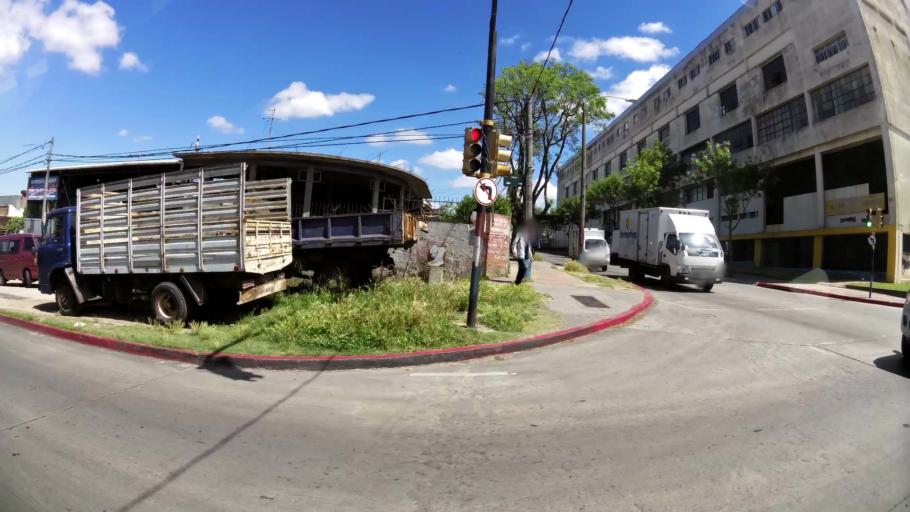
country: UY
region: Montevideo
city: Montevideo
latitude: -34.8542
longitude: -56.1400
